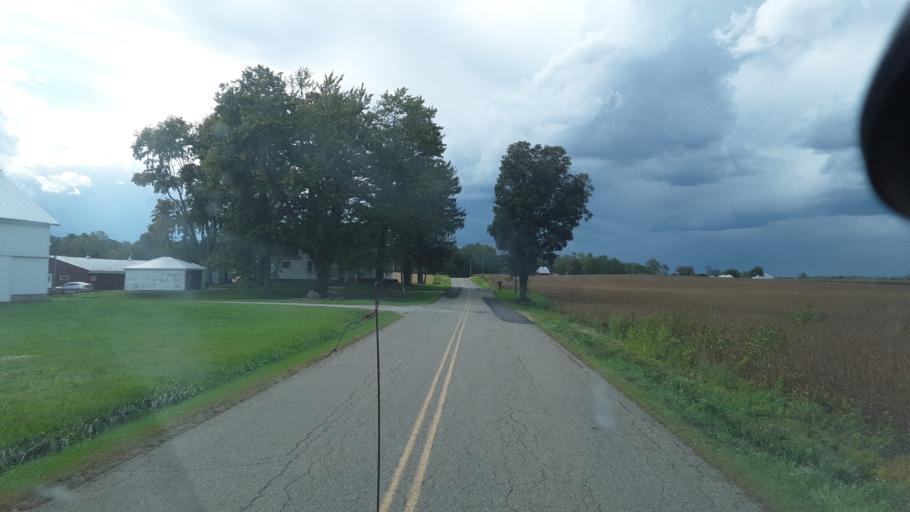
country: US
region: Ohio
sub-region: Knox County
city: Centerburg
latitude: 40.2914
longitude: -82.6461
